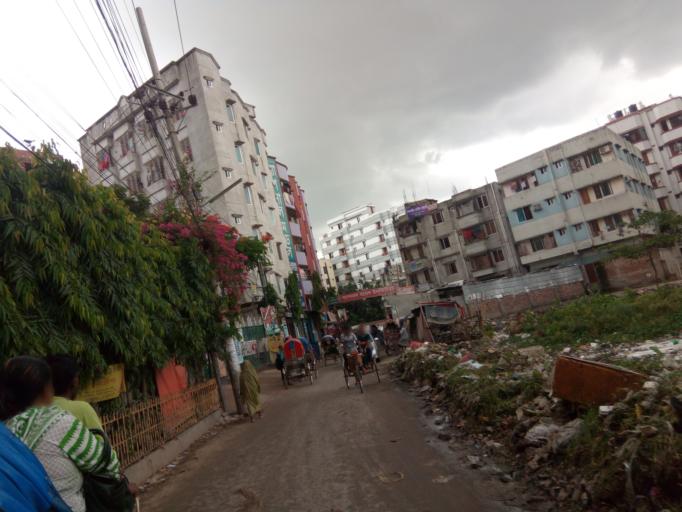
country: BD
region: Dhaka
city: Azimpur
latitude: 23.7626
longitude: 90.3522
